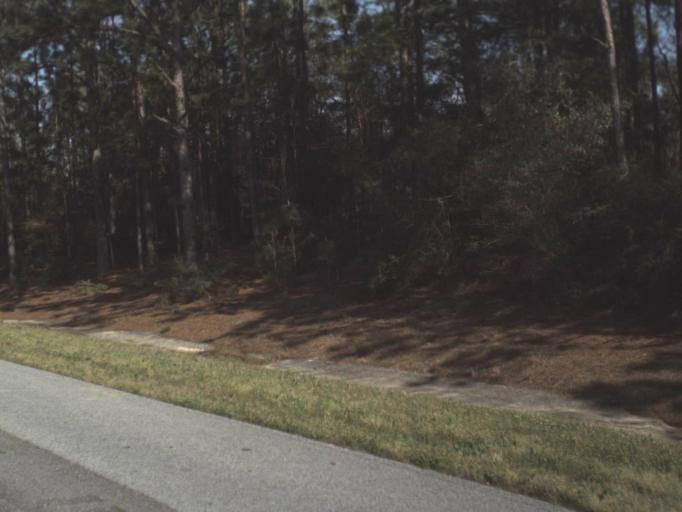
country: US
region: Florida
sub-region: Okaloosa County
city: Crestview
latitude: 30.7199
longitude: -86.4257
